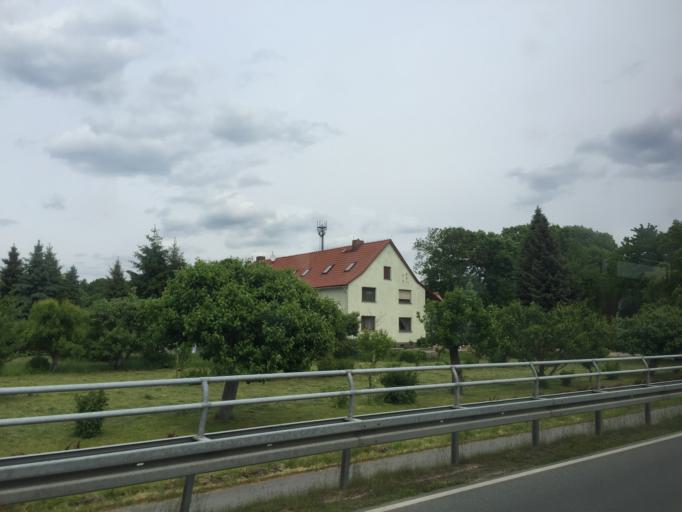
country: DE
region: Saxony
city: Reichenbach
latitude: 51.1460
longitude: 14.8417
